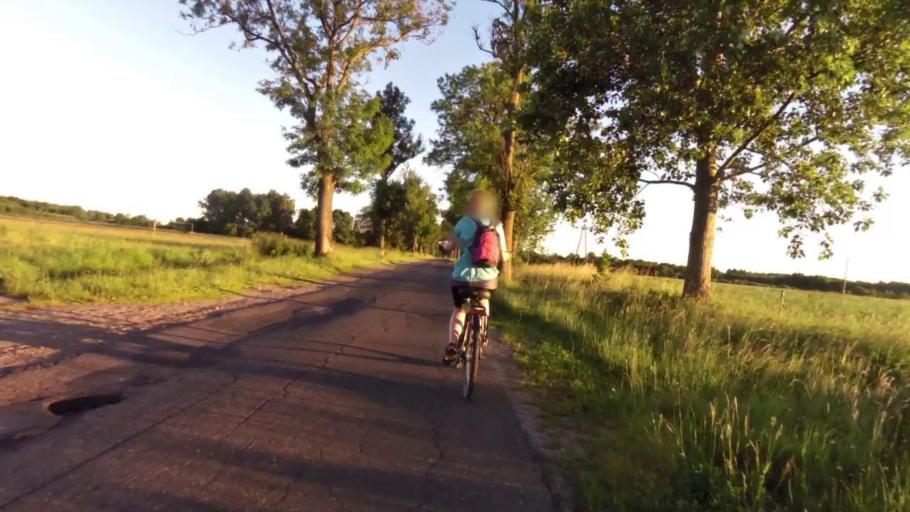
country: PL
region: West Pomeranian Voivodeship
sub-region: Powiat bialogardzki
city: Bialogard
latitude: 54.0505
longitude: 16.0572
